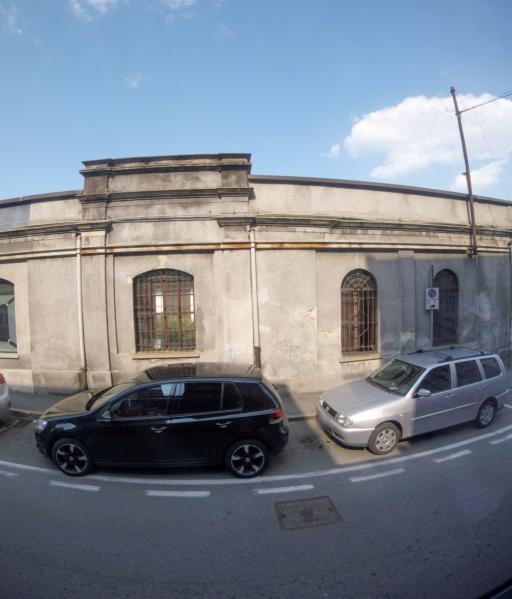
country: IT
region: Piedmont
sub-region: Provincia di Novara
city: Arona
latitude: 45.7571
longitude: 8.5568
